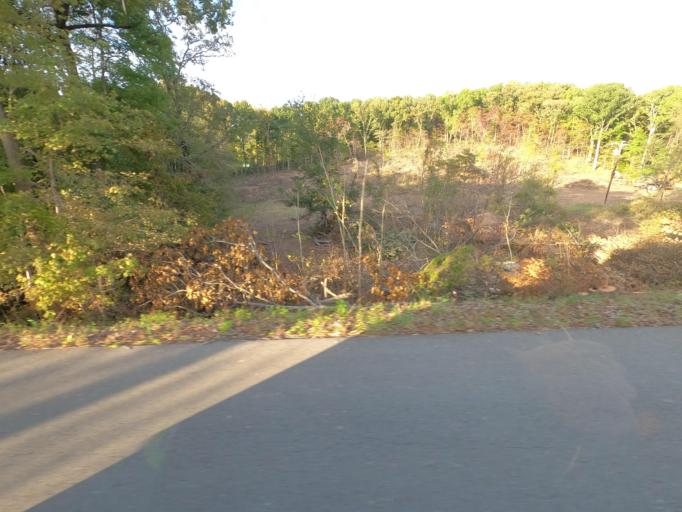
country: US
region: Tennessee
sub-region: Humphreys County
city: Waverly
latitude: 35.8815
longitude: -87.7956
